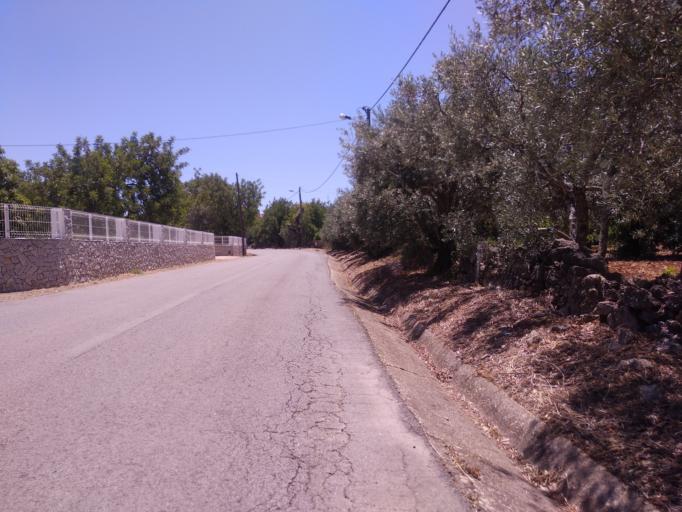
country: PT
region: Faro
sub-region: Sao Bras de Alportel
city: Sao Bras de Alportel
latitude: 37.1700
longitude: -7.8863
